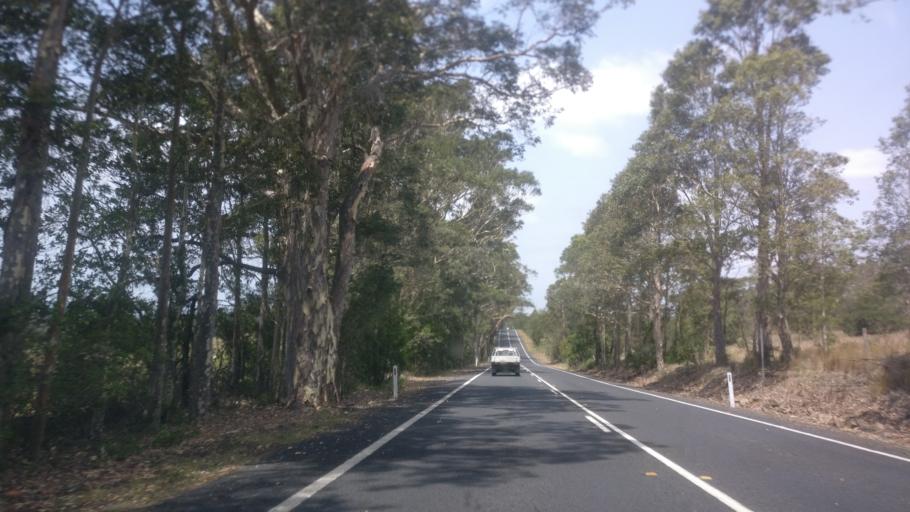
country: AU
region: New South Wales
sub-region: Shoalhaven Shire
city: Bomaderry
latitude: -34.8261
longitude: 150.5730
